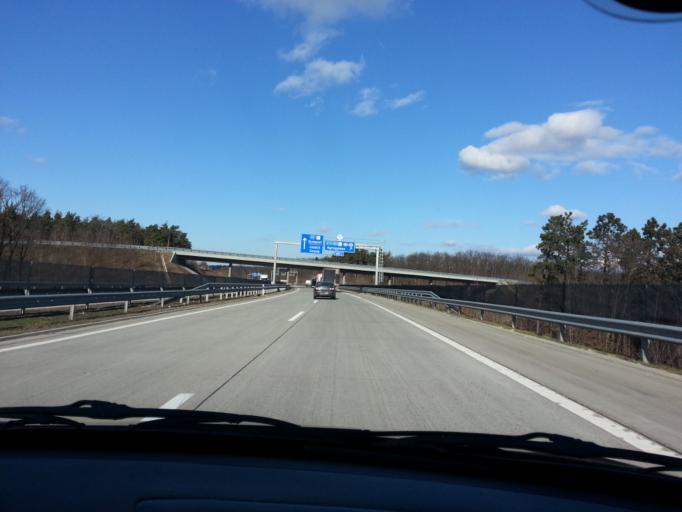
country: HU
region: Pest
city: Szada
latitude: 47.6006
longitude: 19.3210
